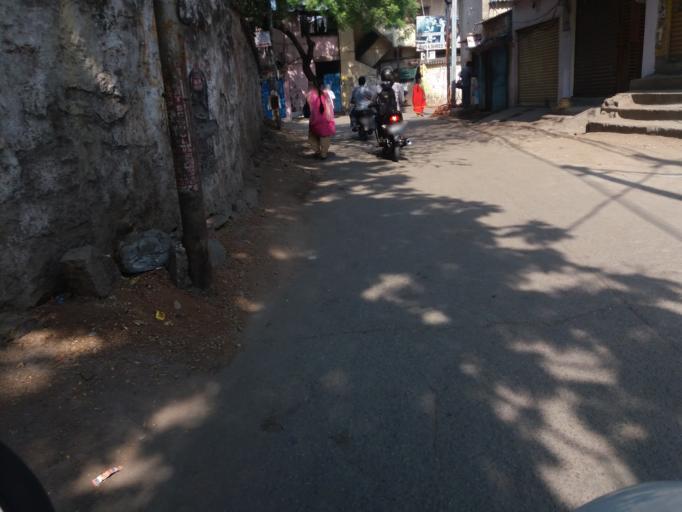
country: IN
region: Telangana
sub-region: Hyderabad
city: Malkajgiri
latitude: 17.4155
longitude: 78.5104
